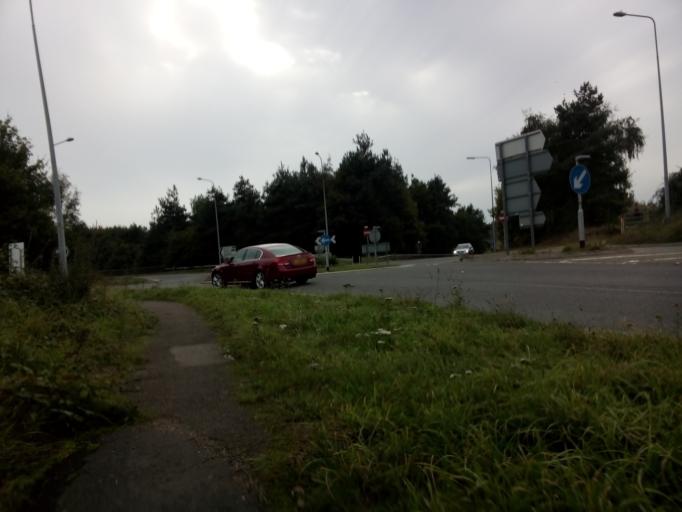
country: GB
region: England
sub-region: Suffolk
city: Ipswich
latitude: 52.0253
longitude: 1.1399
